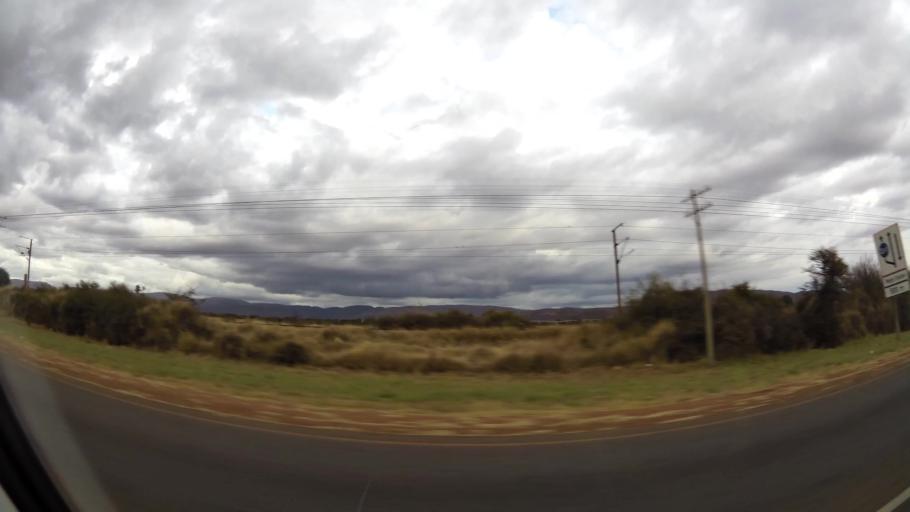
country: ZA
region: Limpopo
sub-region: Waterberg District Municipality
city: Mokopane
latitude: -24.2656
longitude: 28.9836
